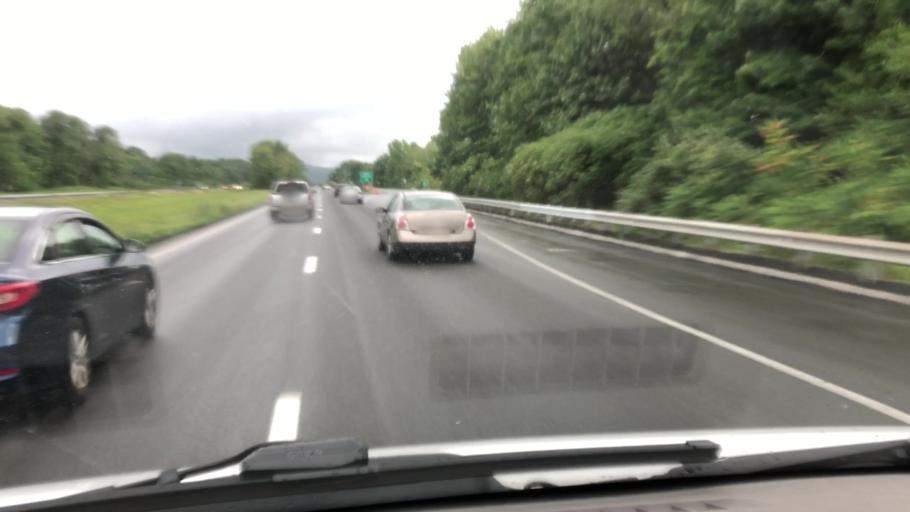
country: US
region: Massachusetts
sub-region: Franklin County
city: South Deerfield
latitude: 42.5016
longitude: -72.6188
